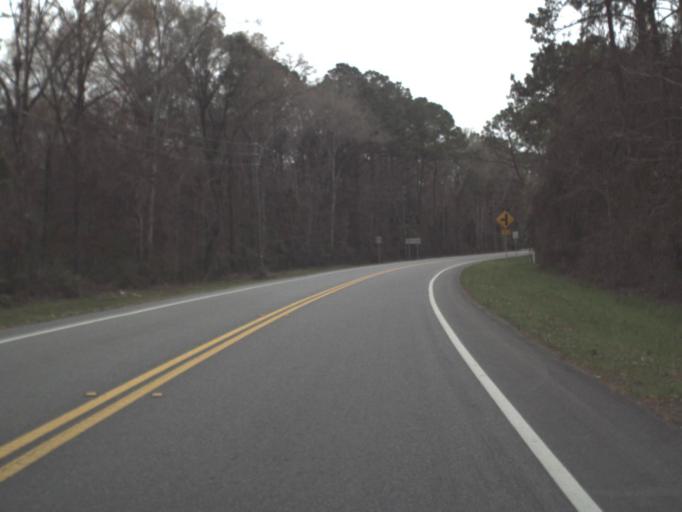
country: US
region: Florida
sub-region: Leon County
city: Woodville
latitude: 30.1989
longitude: -84.1864
